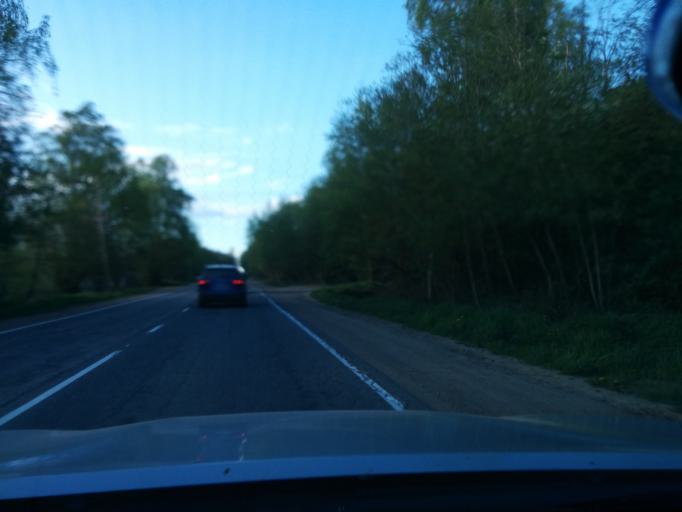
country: RU
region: Leningrad
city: Verkhniye Osel'ki
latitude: 60.2358
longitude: 30.4373
